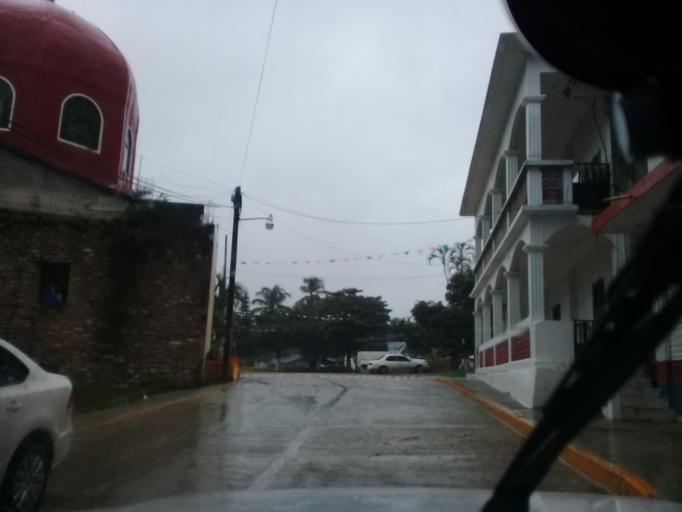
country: MX
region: Veracruz
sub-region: Chalma
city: San Pedro Coyutla
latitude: 21.2302
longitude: -98.4598
